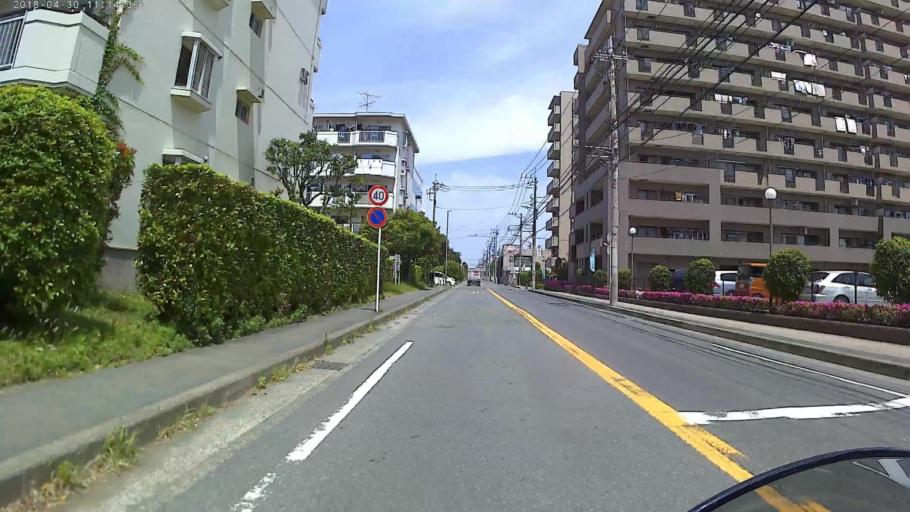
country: JP
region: Kanagawa
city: Minami-rinkan
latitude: 35.4751
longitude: 139.4315
